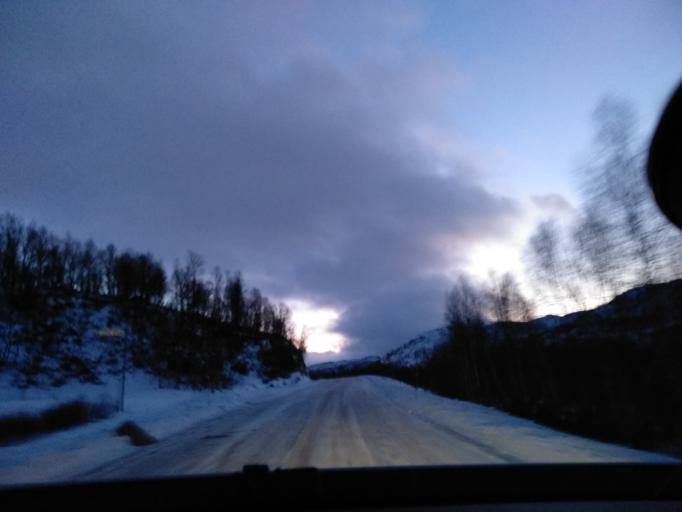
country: NO
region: Vest-Agder
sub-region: Sirdal
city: Tonstad
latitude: 59.0175
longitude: 6.9378
